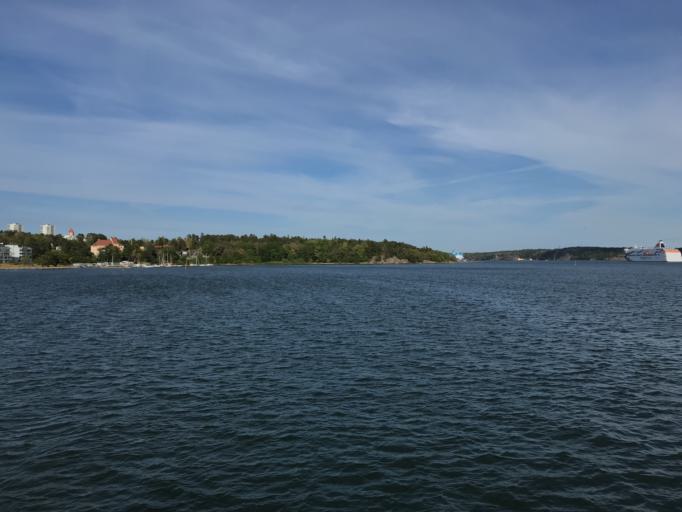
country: SE
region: Stockholm
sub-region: Nacka Kommun
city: Nacka
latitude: 59.3404
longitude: 18.1524
